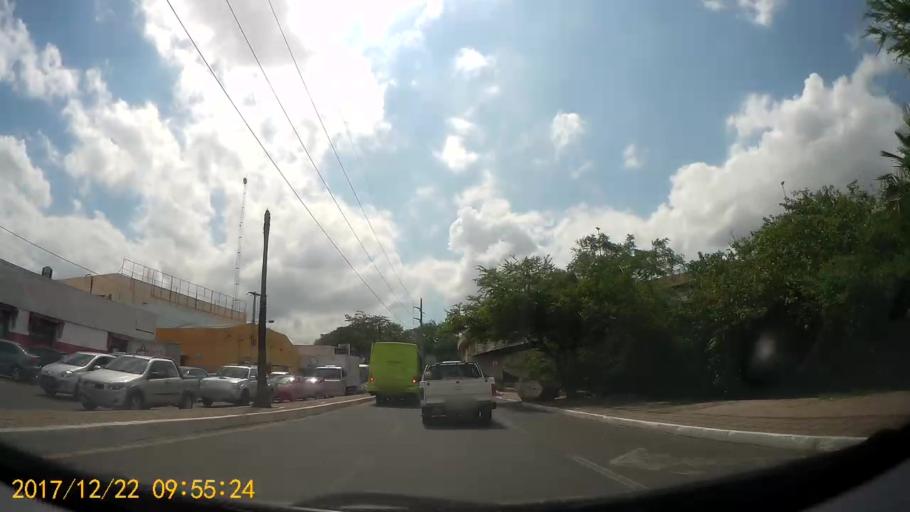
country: BR
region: Piaui
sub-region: Teresina
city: Teresina
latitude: -5.0970
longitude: -42.8161
